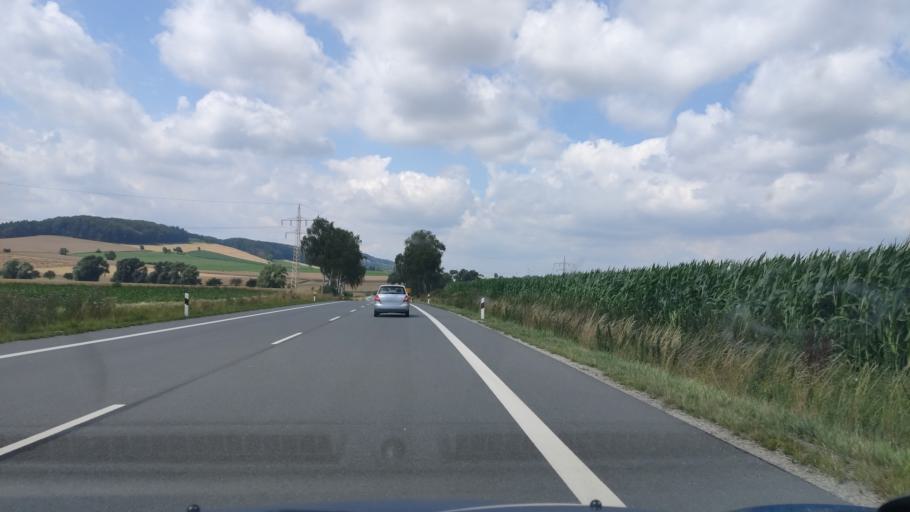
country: DE
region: Lower Saxony
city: Dielmissen
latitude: 51.9700
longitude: 9.5961
